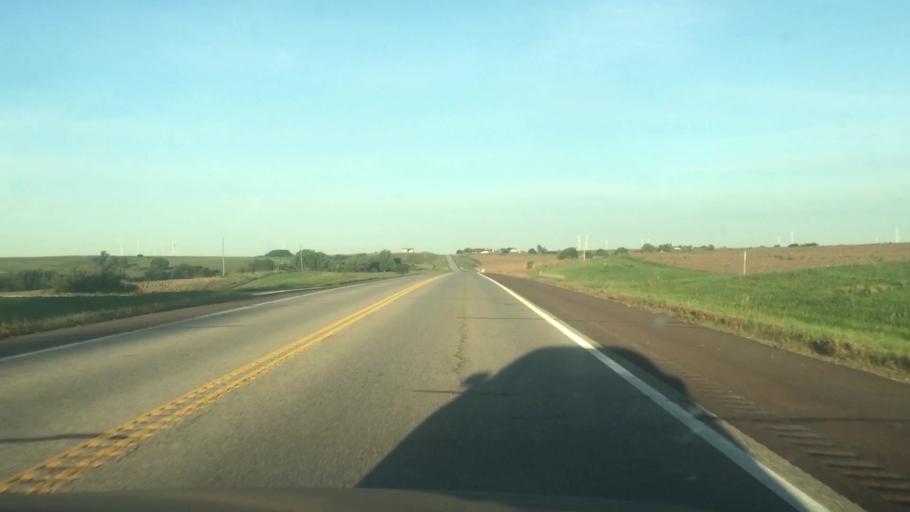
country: US
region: Kansas
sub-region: Nemaha County
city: Seneca
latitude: 39.8421
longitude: -96.2981
